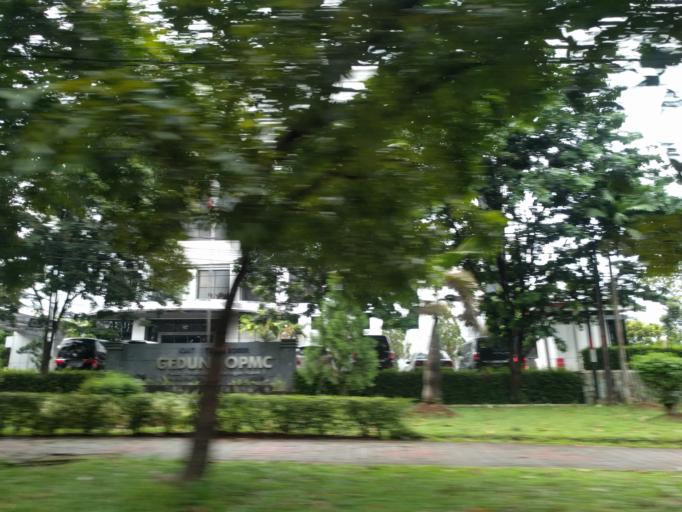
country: ID
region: West Java
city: Bogor
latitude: -6.5866
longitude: 106.8055
